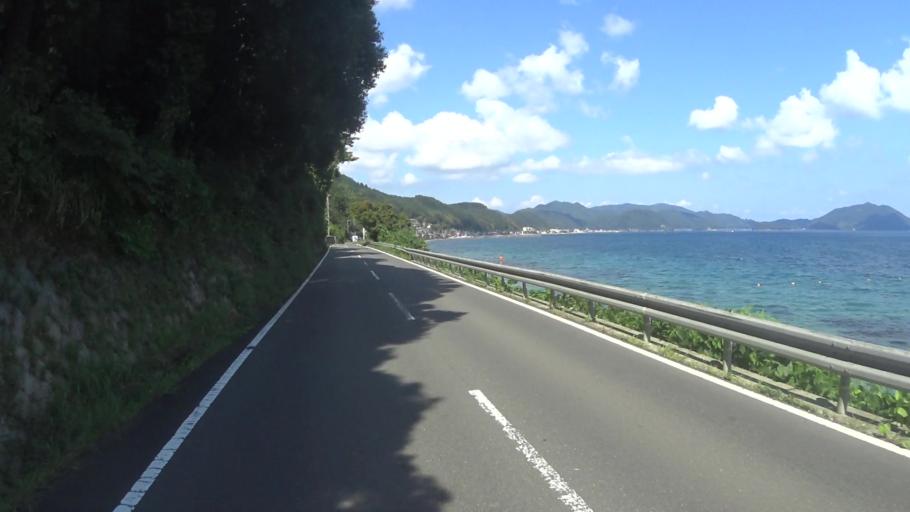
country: JP
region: Kyoto
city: Miyazu
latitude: 35.6404
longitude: 135.2503
